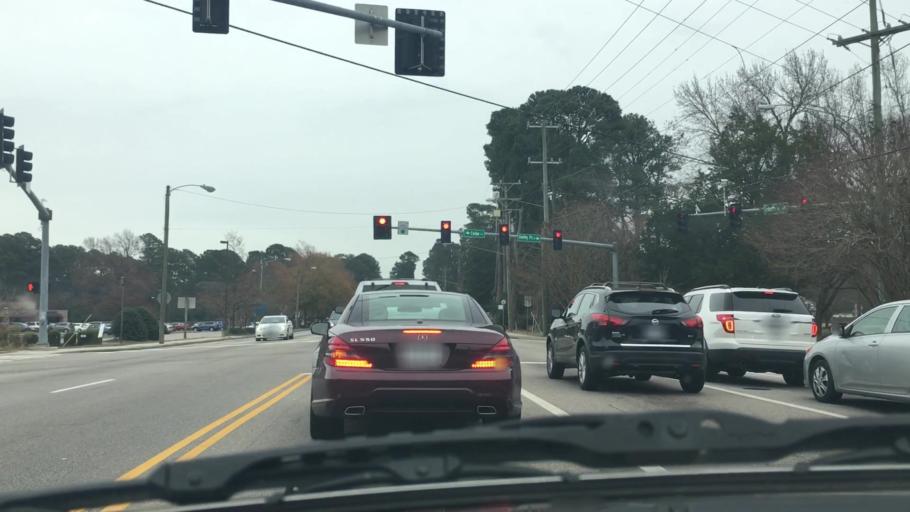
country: US
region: Virginia
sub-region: City of Portsmouth
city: Portsmouth Heights
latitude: 36.8521
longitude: -76.3794
